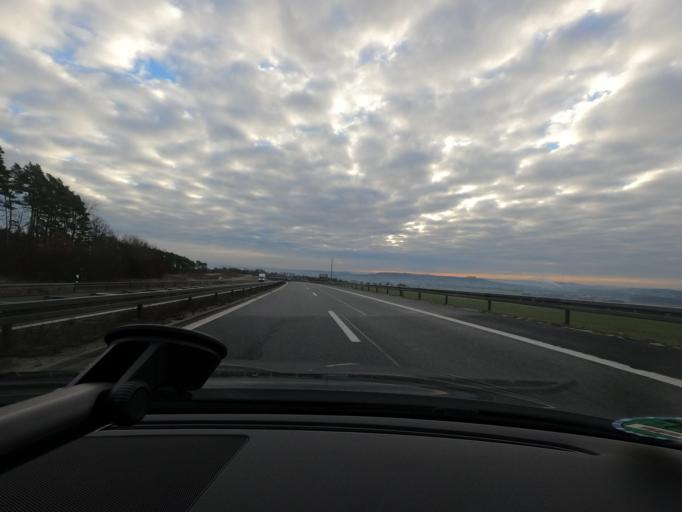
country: DE
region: Bavaria
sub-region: Upper Franconia
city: Lautertal
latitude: 50.3236
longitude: 10.9463
